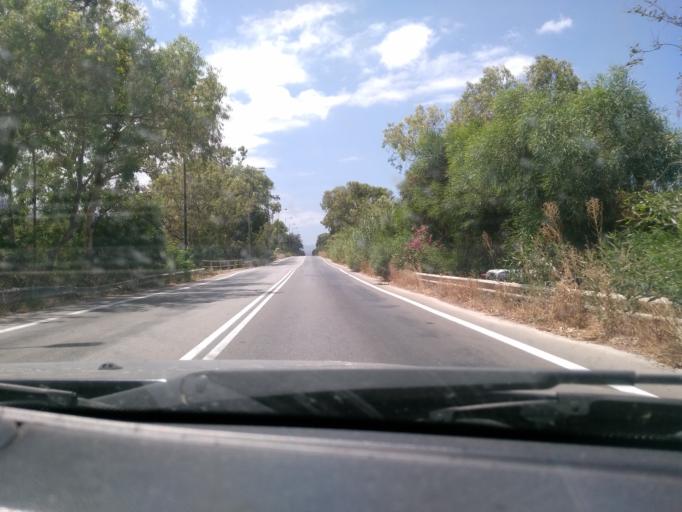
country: GR
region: Crete
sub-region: Nomos Chanias
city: Georgioupolis
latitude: 35.3519
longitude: 24.2909
